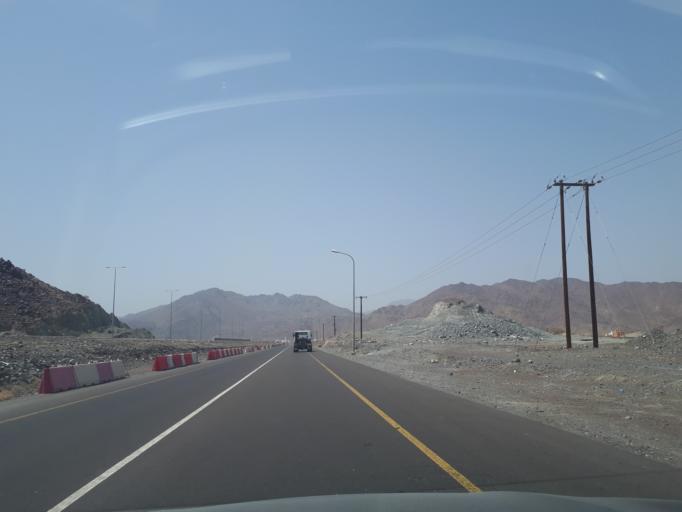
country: OM
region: Muhafazat ad Dakhiliyah
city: Sufalat Sama'il
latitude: 23.2762
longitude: 58.1061
